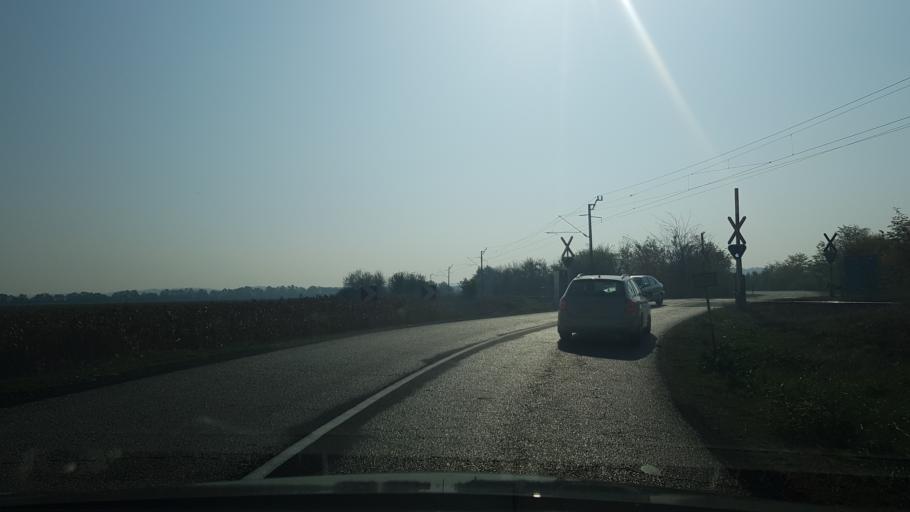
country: HU
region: Fejer
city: Adony
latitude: 47.0968
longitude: 18.8561
